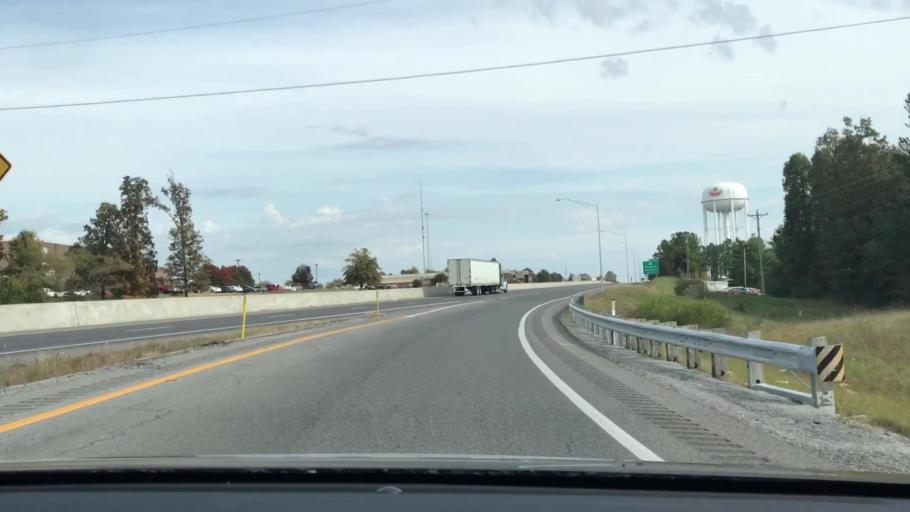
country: US
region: Kentucky
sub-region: Graves County
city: Mayfield
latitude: 36.7587
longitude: -88.6539
